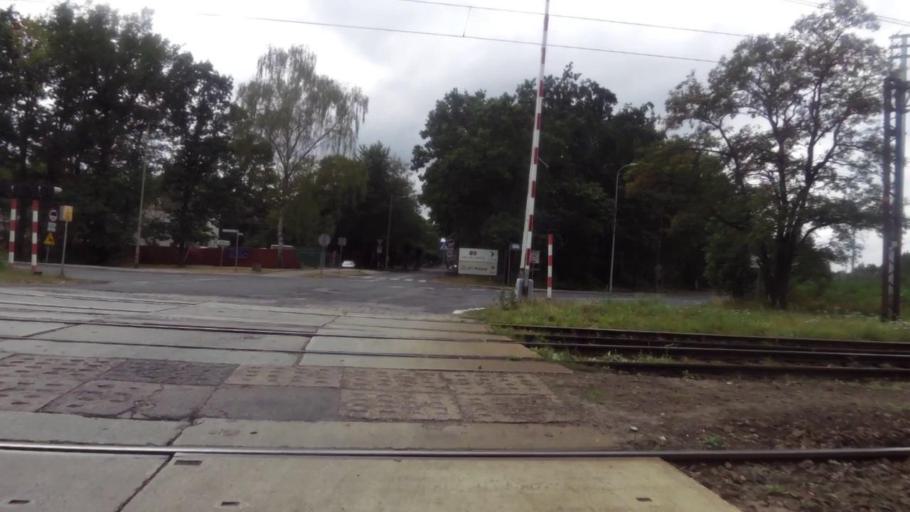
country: PL
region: Lubusz
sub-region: Powiat gorzowski
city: Kostrzyn nad Odra
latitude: 52.6088
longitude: 14.6424
